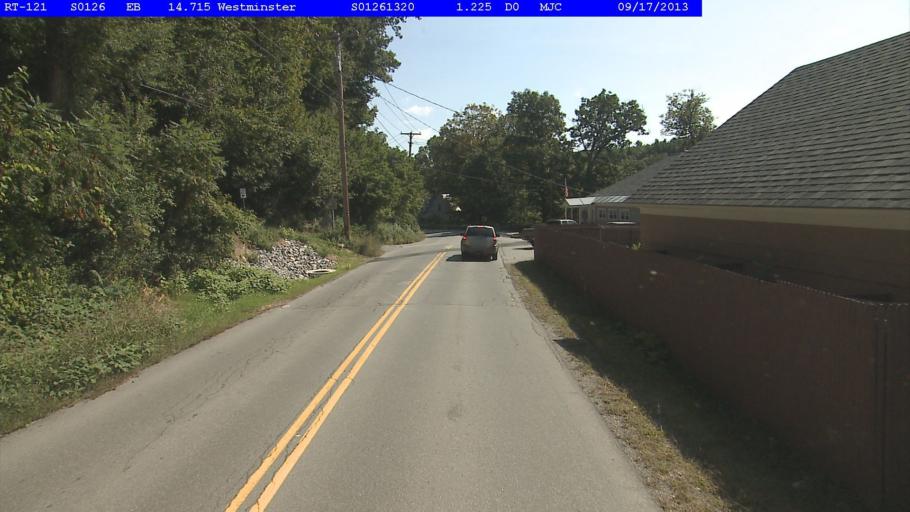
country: US
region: Vermont
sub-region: Windham County
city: Bellows Falls
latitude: 43.1189
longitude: -72.4557
